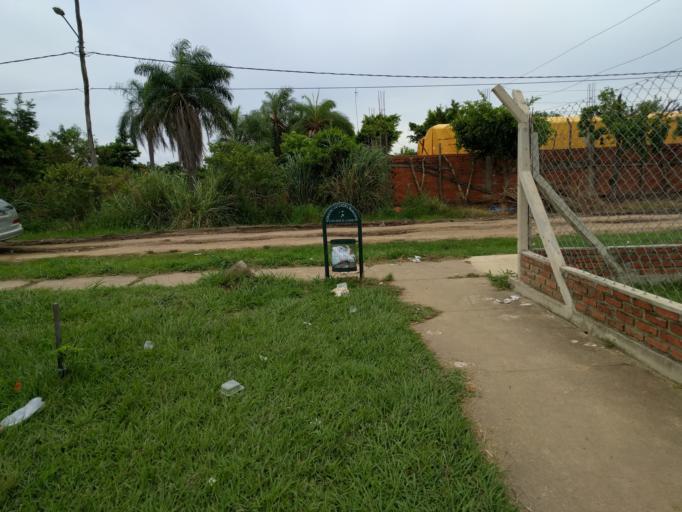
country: BO
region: Santa Cruz
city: Santa Cruz de la Sierra
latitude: -17.8467
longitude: -63.2351
